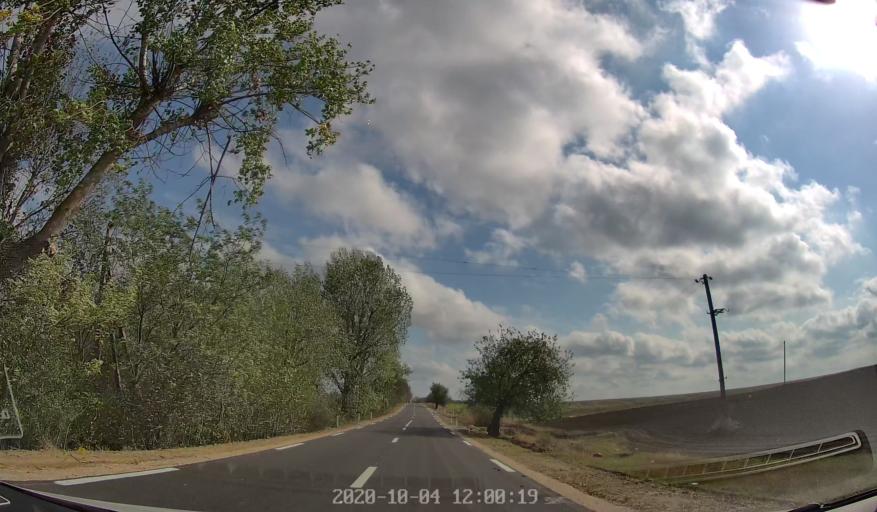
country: MD
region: Rezina
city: Saharna
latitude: 47.6312
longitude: 28.8697
